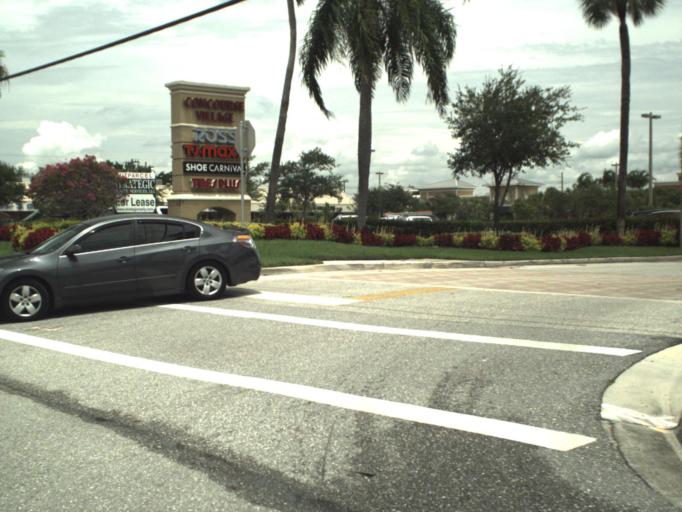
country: US
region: Florida
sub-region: Palm Beach County
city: Jupiter
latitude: 26.9342
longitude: -80.0914
